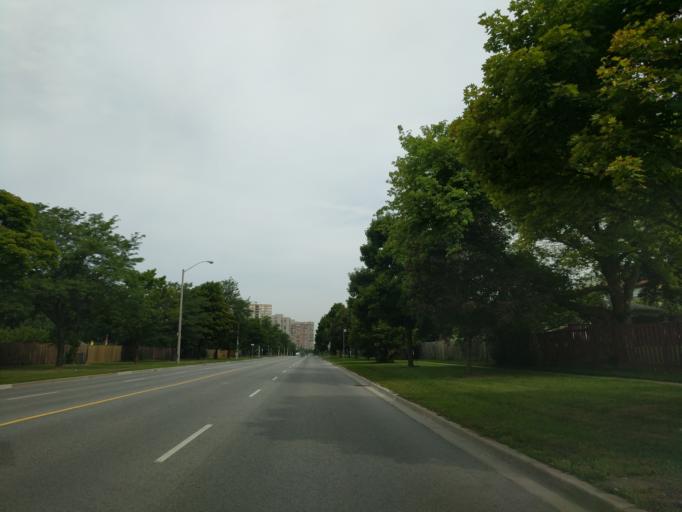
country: CA
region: Ontario
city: Scarborough
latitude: 43.8080
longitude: -79.3217
